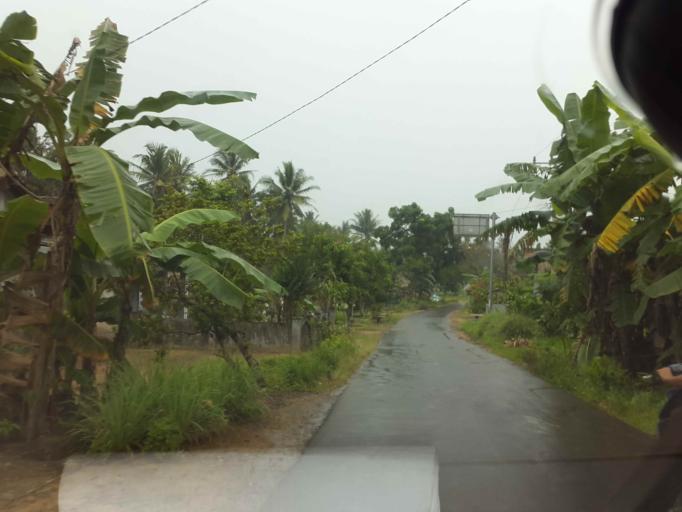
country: ID
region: Lampung
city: Panjang
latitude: -5.4588
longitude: 105.3880
